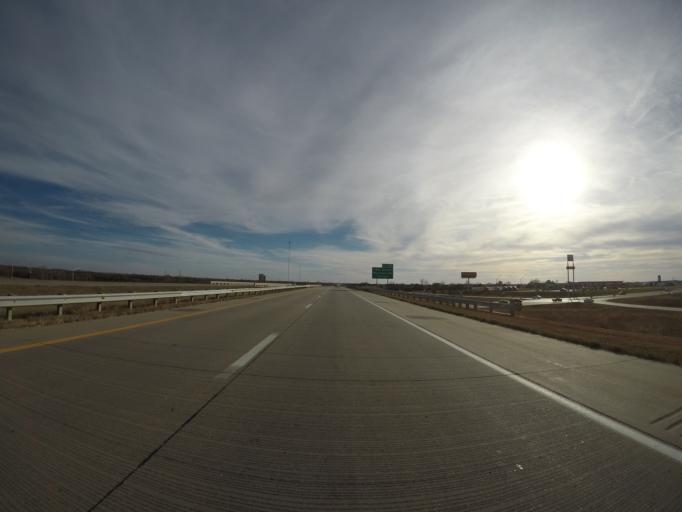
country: US
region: Kansas
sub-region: Franklin County
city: Ottawa
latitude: 38.6240
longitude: -95.2324
